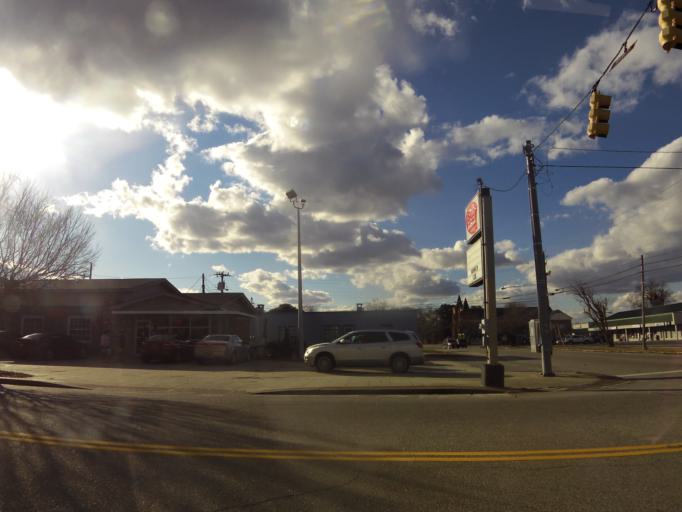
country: US
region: South Carolina
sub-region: Clarendon County
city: Manning
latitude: 33.6965
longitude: -80.2107
